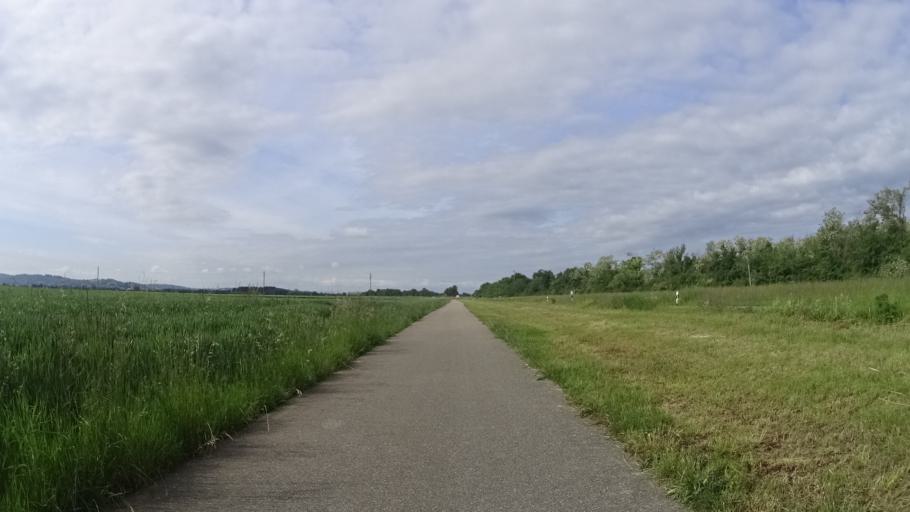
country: DE
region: Baden-Wuerttemberg
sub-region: Freiburg Region
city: Neuenburg am Rhein
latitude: 47.8003
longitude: 7.5601
